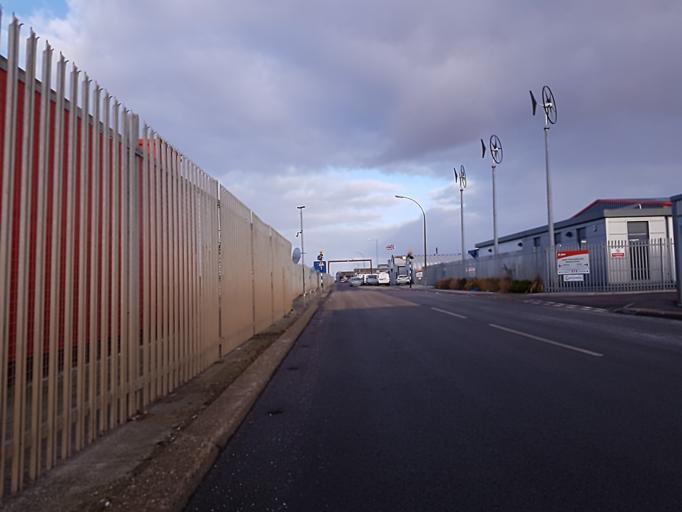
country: GB
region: England
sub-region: North East Lincolnshire
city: Grimsby
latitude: 53.5787
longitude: -0.0579
